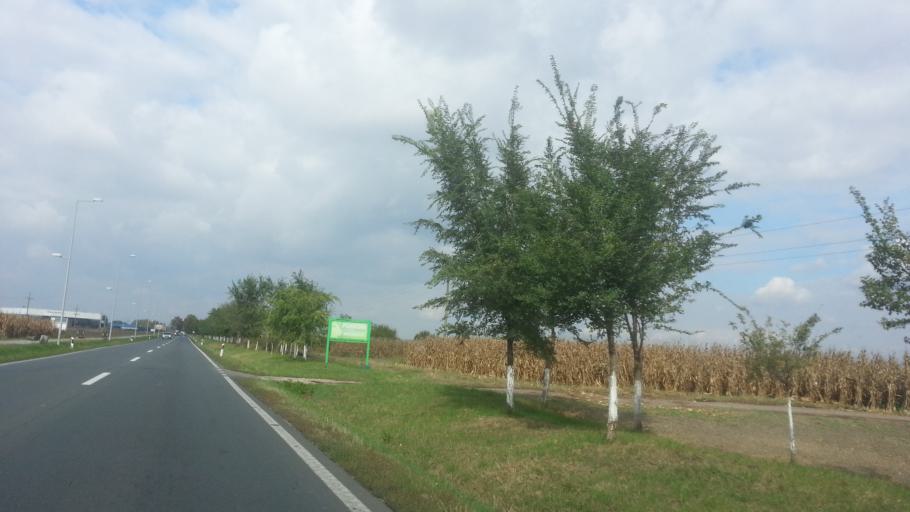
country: RS
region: Autonomna Pokrajina Vojvodina
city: Nova Pazova
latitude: 44.9620
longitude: 20.1920
